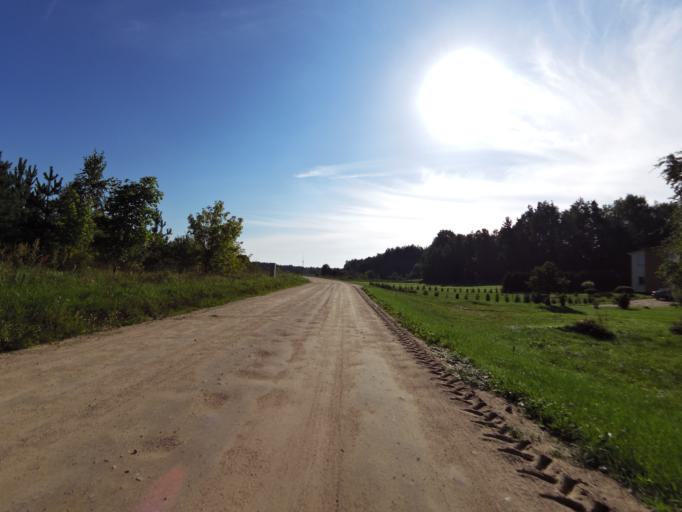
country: LT
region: Vilnius County
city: Pilaite
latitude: 54.7017
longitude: 25.1337
